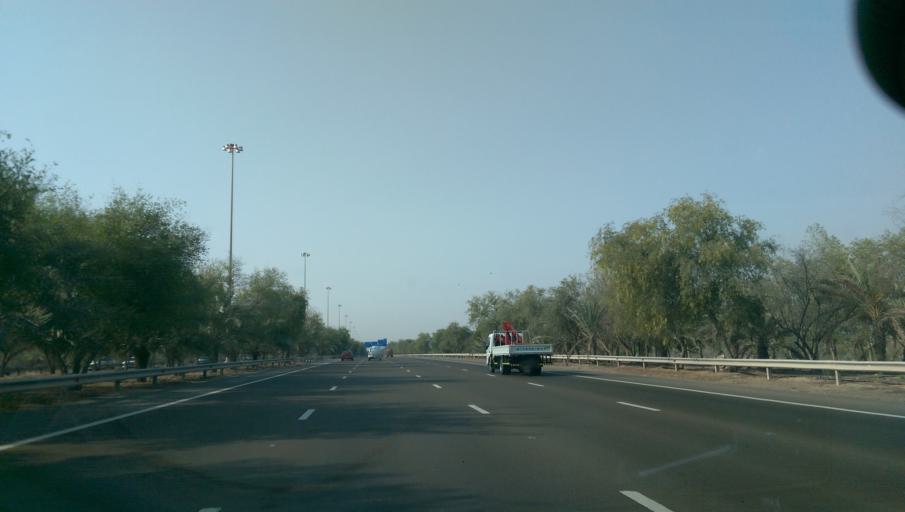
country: AE
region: Abu Dhabi
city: Abu Dhabi
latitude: 24.4779
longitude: 54.6755
